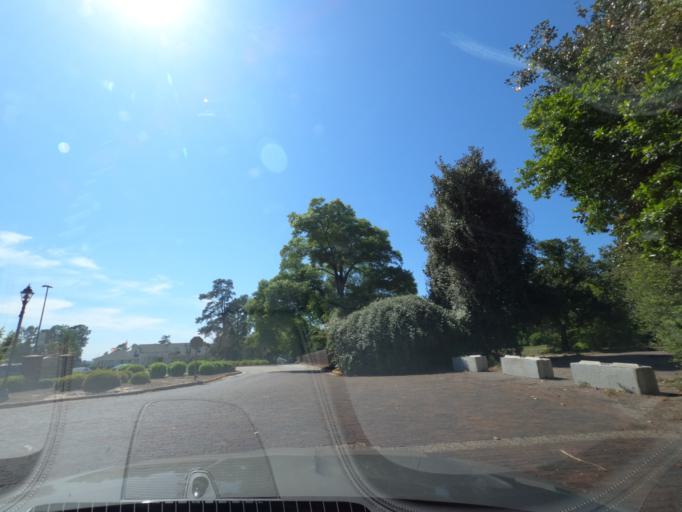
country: US
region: Georgia
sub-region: Columbia County
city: Martinez
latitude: 33.4731
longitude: -82.0466
